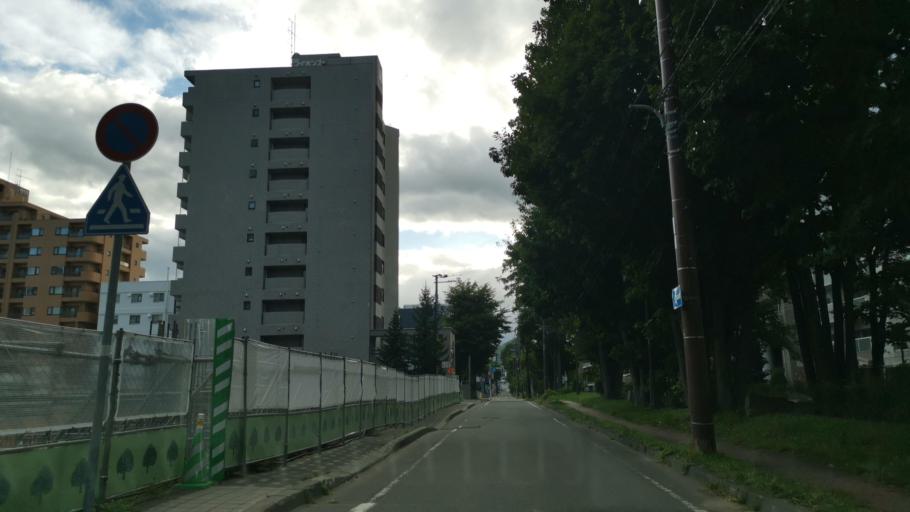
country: JP
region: Hokkaido
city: Sapporo
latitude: 43.0634
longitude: 141.3352
